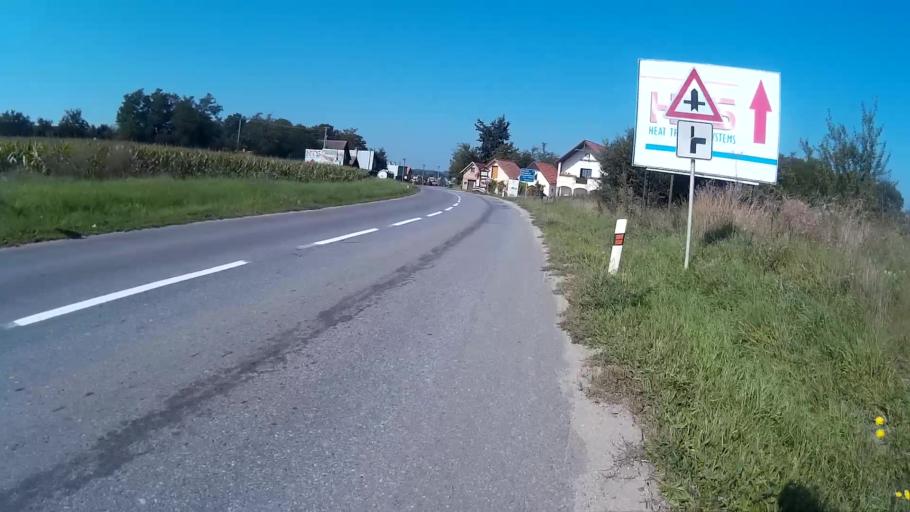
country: CZ
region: South Moravian
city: Novosedly
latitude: 48.8363
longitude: 16.5083
